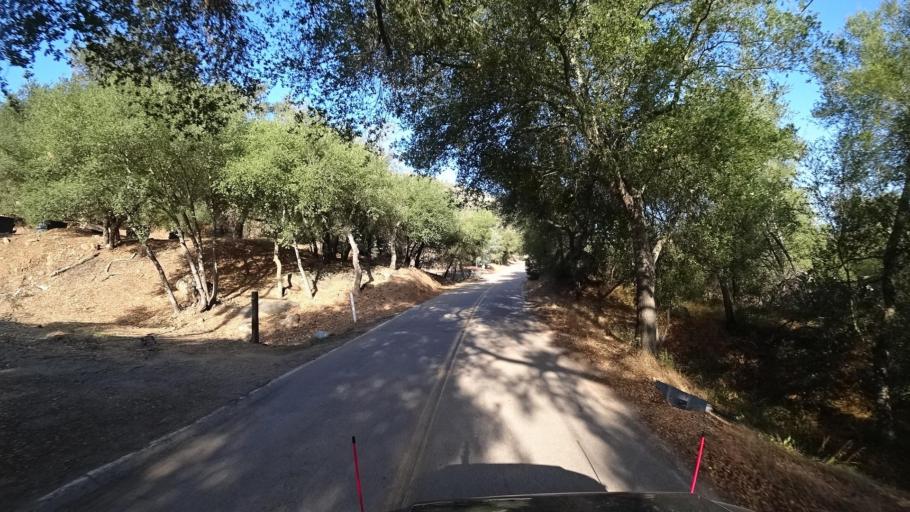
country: US
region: California
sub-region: San Diego County
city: Valley Center
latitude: 33.1659
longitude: -116.9964
